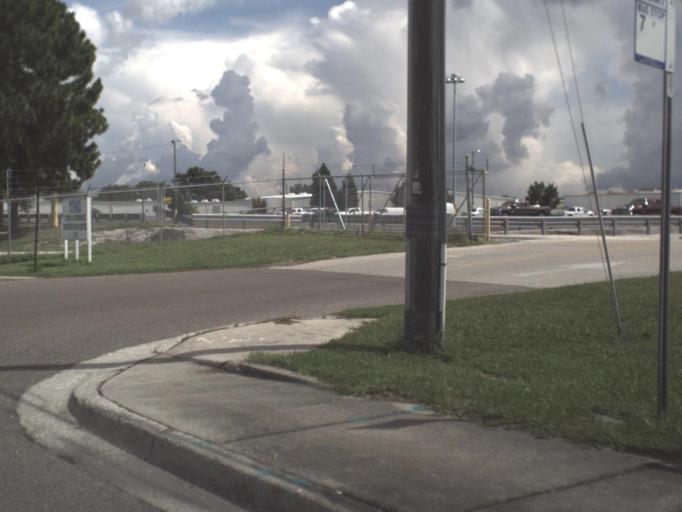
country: US
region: Florida
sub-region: Hillsborough County
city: Egypt Lake-Leto
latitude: 28.0135
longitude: -82.5332
